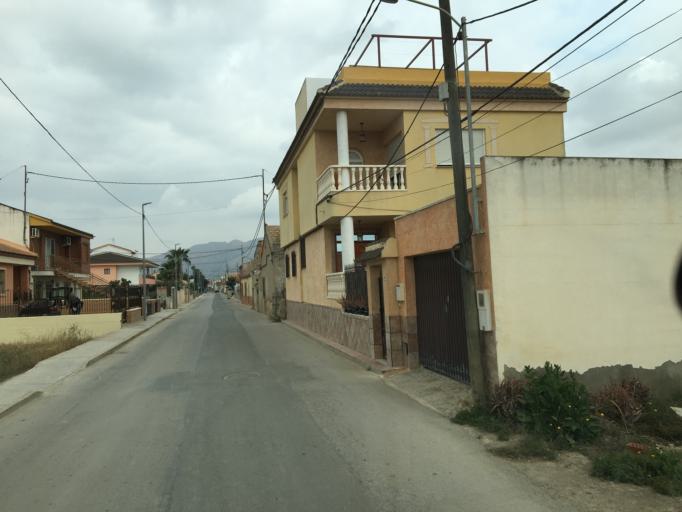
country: ES
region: Murcia
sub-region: Murcia
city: Beniel
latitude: 38.0417
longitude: -0.9906
